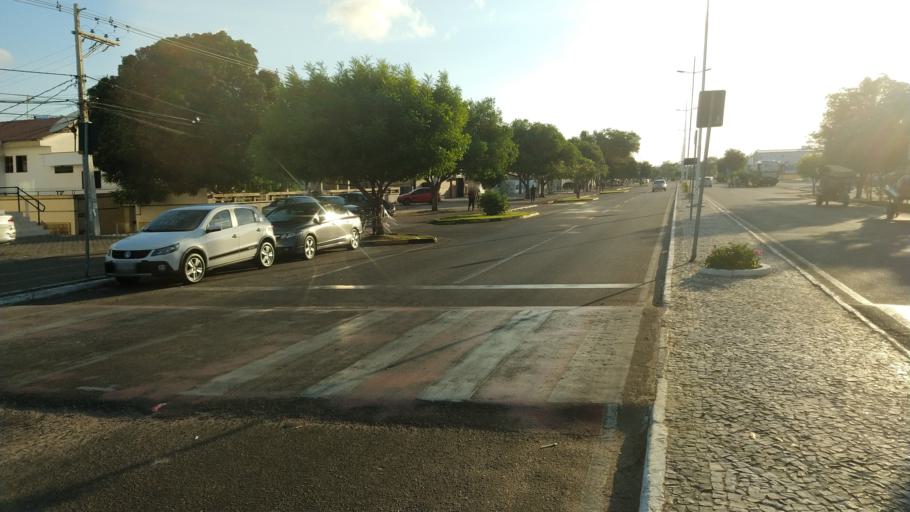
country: BR
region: Bahia
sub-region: Paulo Afonso
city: Paulo Afonso
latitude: -9.3984
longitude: -38.2237
